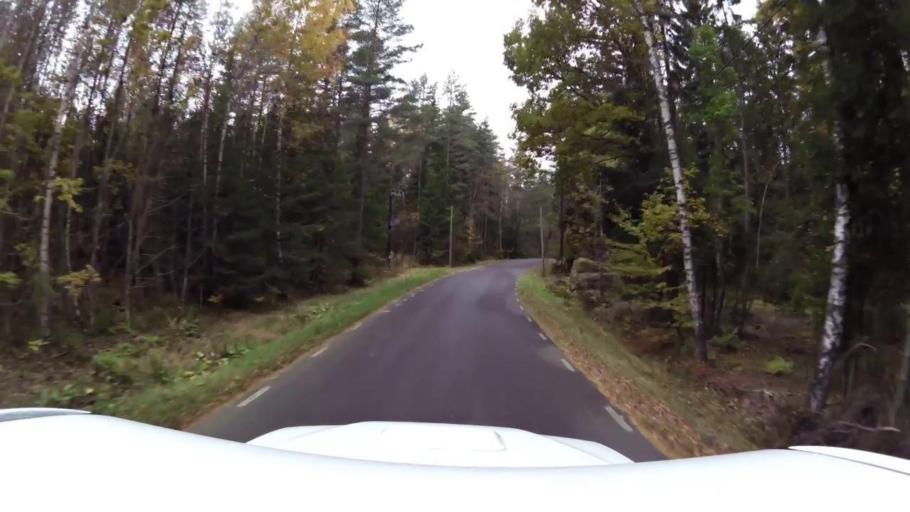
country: SE
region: OEstergoetland
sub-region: Motala Kommun
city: Borensberg
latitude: 58.5601
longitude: 15.3956
